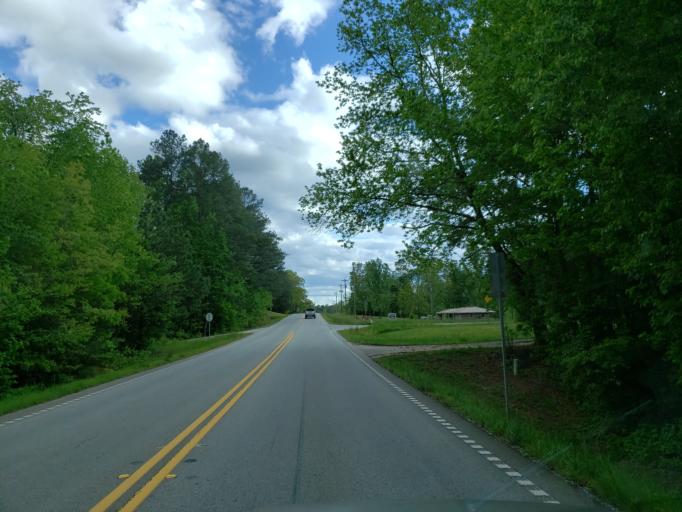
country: US
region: Georgia
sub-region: Haralson County
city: Tallapoosa
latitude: 33.8452
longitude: -85.2924
